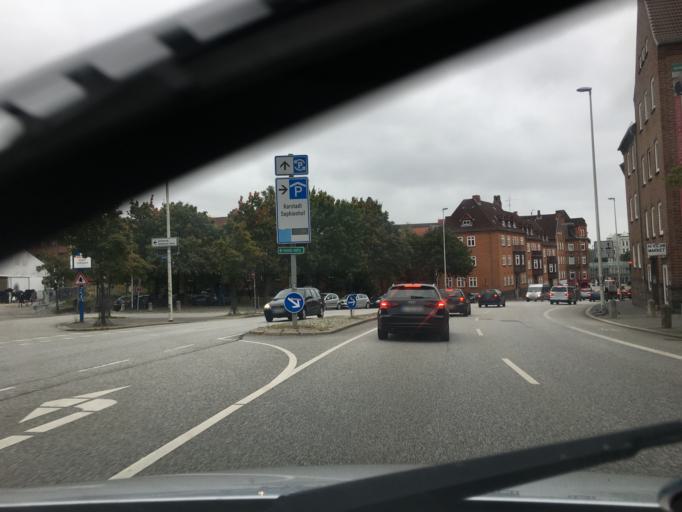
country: DE
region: Schleswig-Holstein
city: Kiel
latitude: 54.3200
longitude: 10.1303
